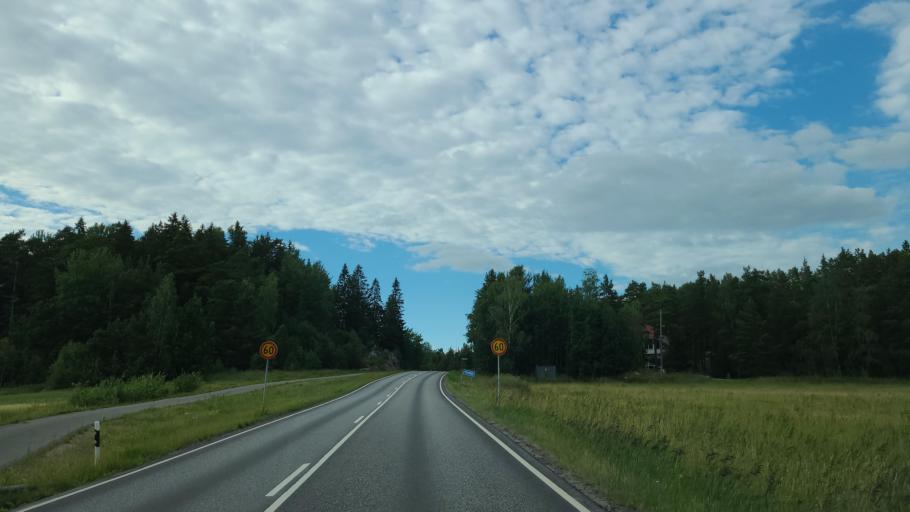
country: FI
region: Varsinais-Suomi
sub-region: Turku
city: Rymaettylae
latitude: 60.4060
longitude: 21.8951
